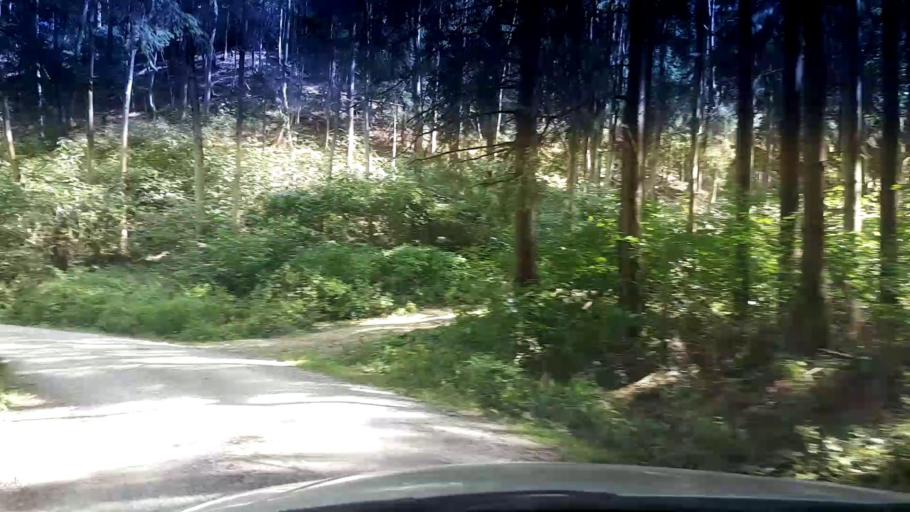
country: DE
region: Bavaria
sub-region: Upper Franconia
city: Schesslitz
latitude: 49.9355
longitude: 11.0647
